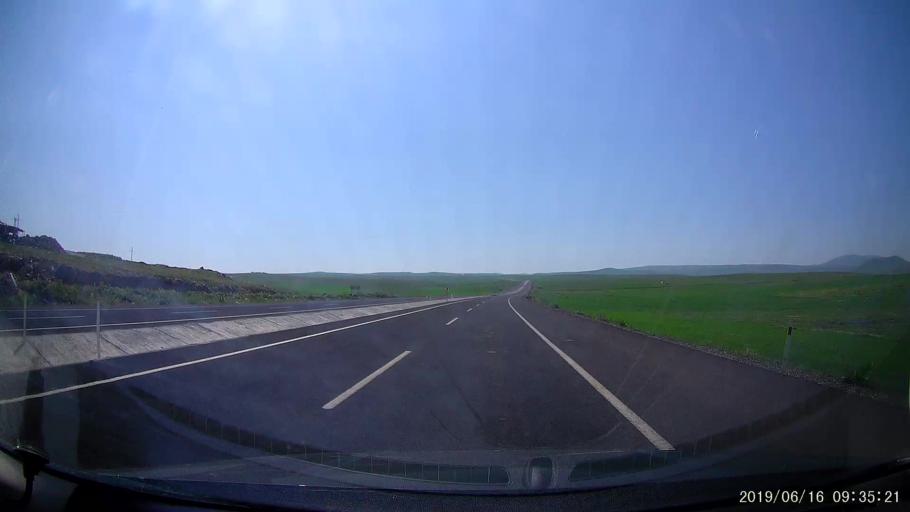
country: TR
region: Kars
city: Kars
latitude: 40.5734
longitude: 43.1544
